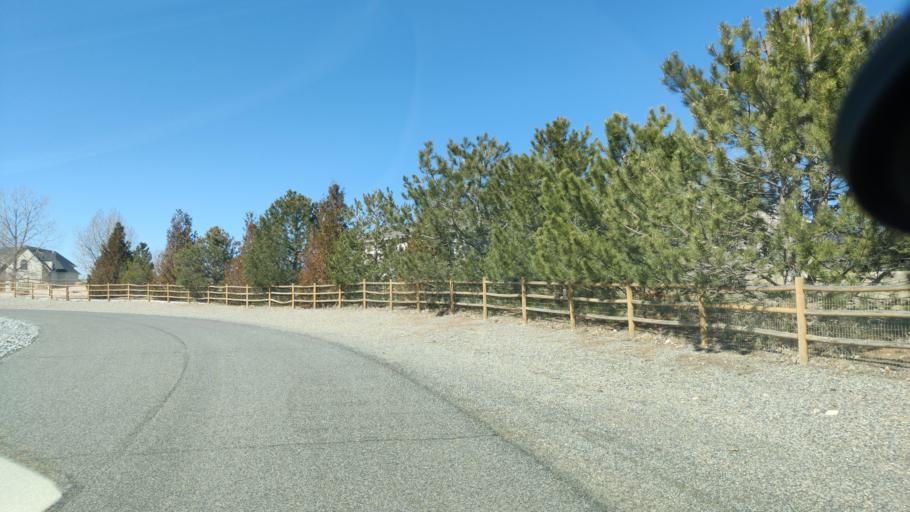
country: US
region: Colorado
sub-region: Mesa County
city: Fruita
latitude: 39.2086
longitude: -108.7095
